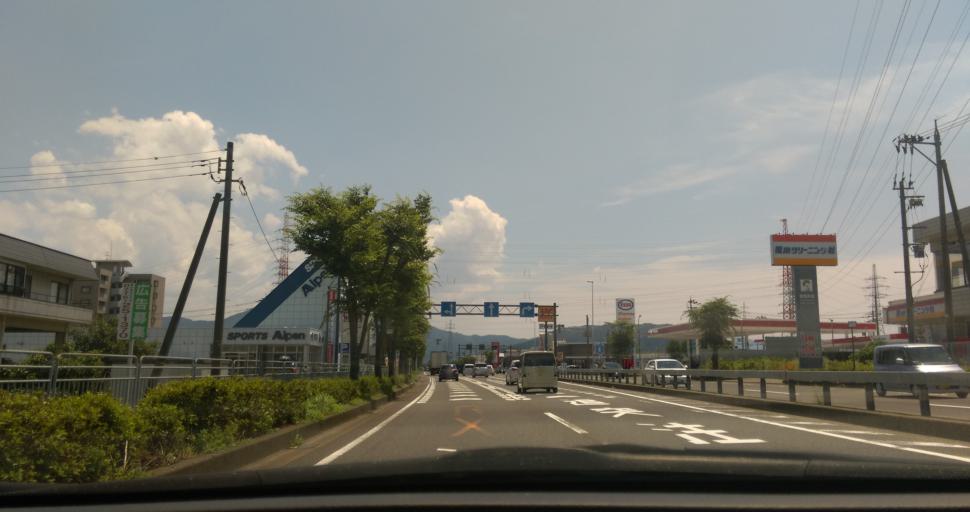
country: JP
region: Fukui
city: Sabae
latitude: 35.9337
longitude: 136.1897
